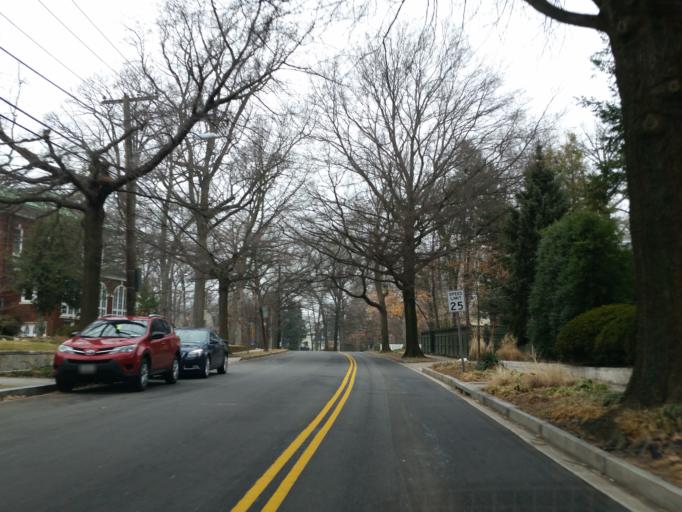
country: US
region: Maryland
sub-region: Montgomery County
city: Chevy Chase Village
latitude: 38.9563
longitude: -77.0737
